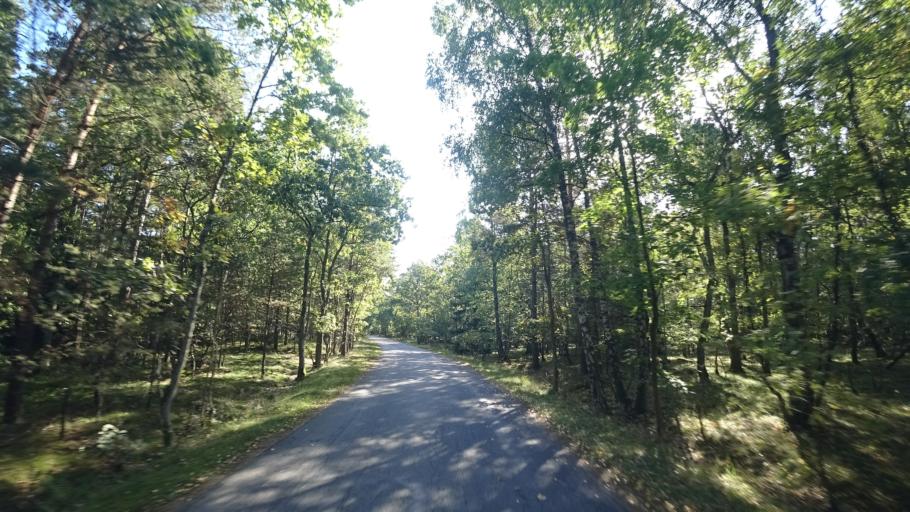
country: SE
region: Skane
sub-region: Kristianstads Kommun
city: Ahus
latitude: 55.9233
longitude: 14.3081
